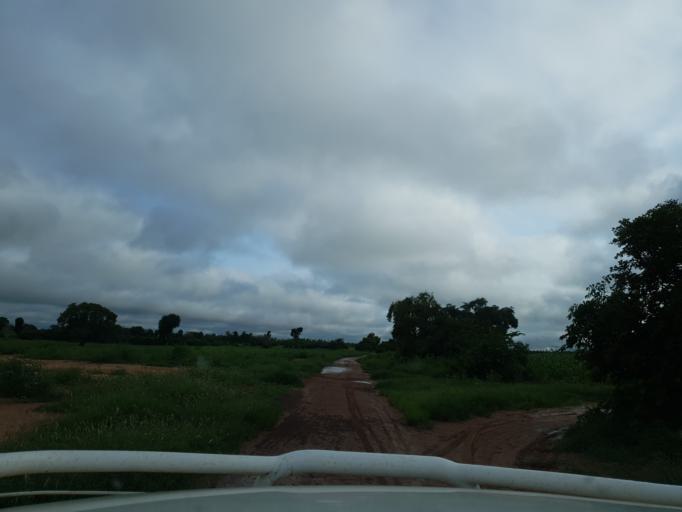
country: ML
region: Segou
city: Baroueli
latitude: 13.4041
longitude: -7.0067
